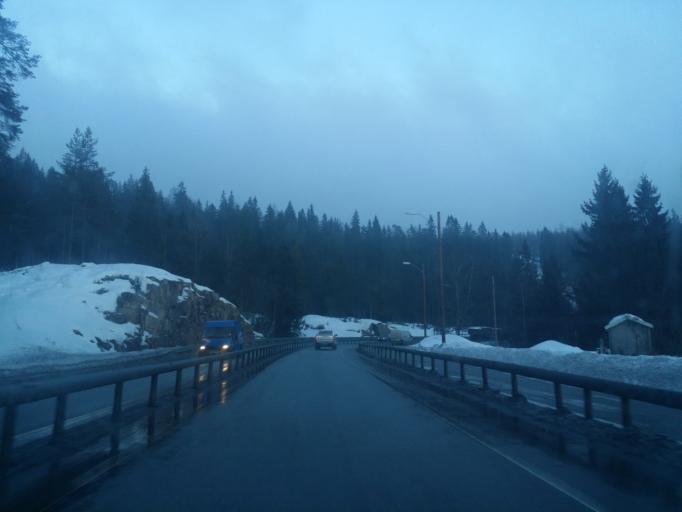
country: NO
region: Buskerud
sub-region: Hole
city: Vik
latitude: 59.9722
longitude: 10.3356
